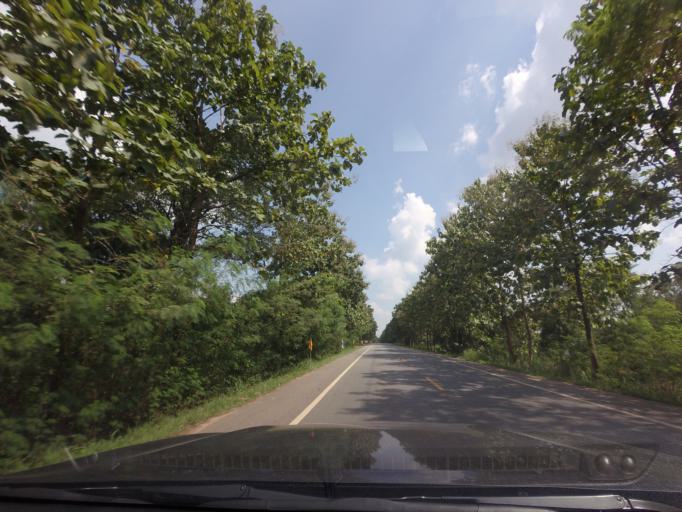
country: TH
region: Phitsanulok
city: Chat Trakan
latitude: 17.2843
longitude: 100.5255
